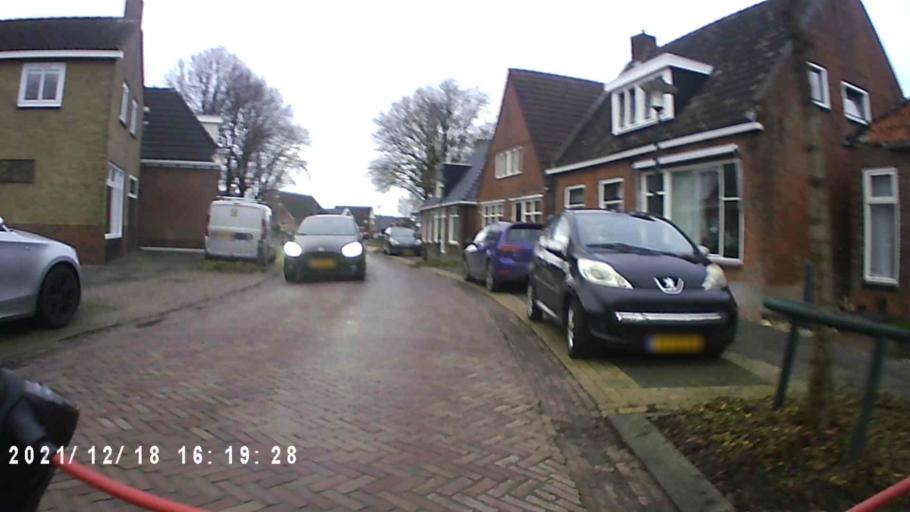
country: NL
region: Friesland
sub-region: Gemeente Dongeradeel
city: Anjum
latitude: 53.3782
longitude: 6.0542
